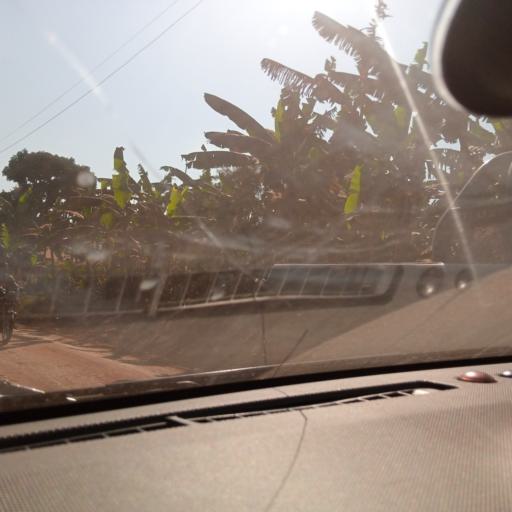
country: UG
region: Central Region
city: Masaka
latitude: -0.3422
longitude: 31.7325
